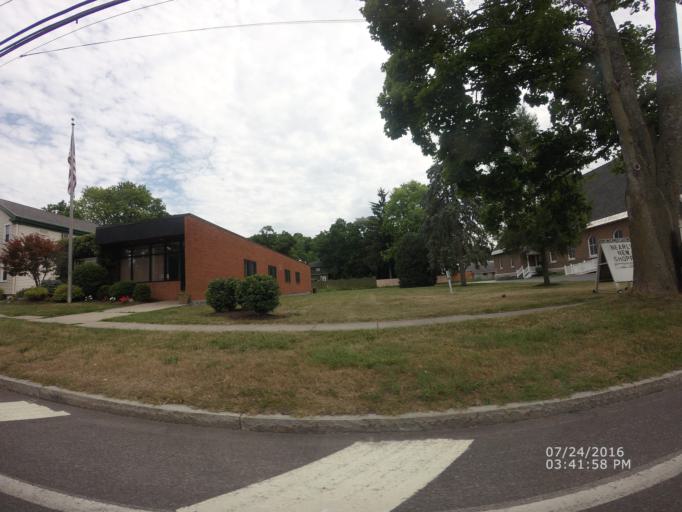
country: US
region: New York
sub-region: Onondaga County
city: Camillus
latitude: 43.0390
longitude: -76.3071
